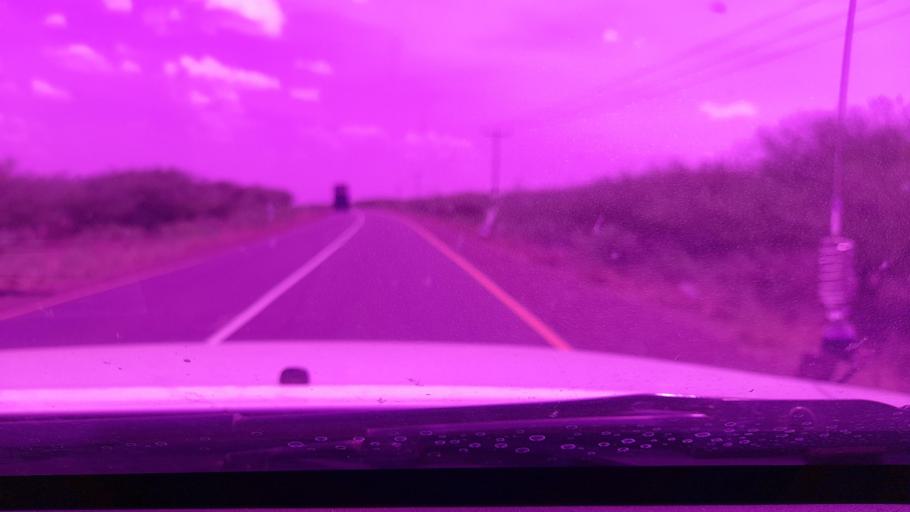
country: ET
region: Afar
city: Awash
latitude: 9.3552
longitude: 40.3036
